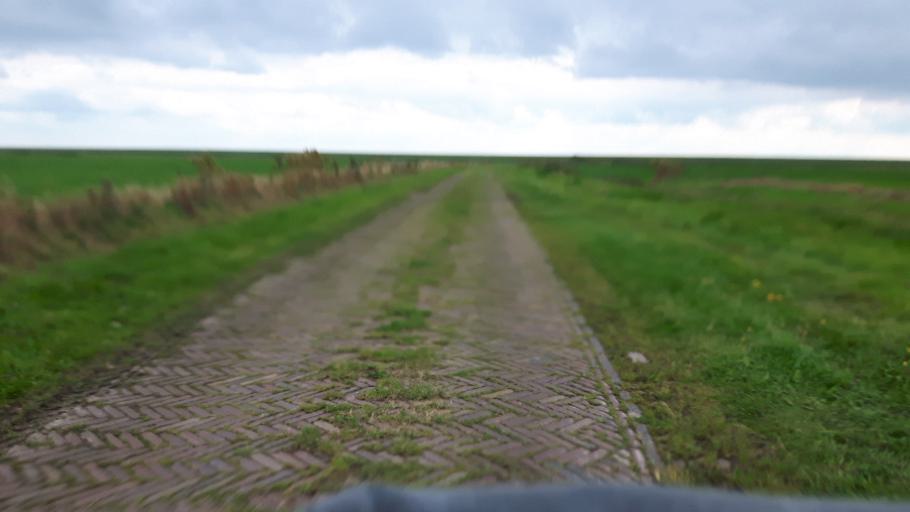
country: NL
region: Friesland
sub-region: Gemeente Ameland
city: Nes
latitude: 53.4451
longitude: 5.8207
